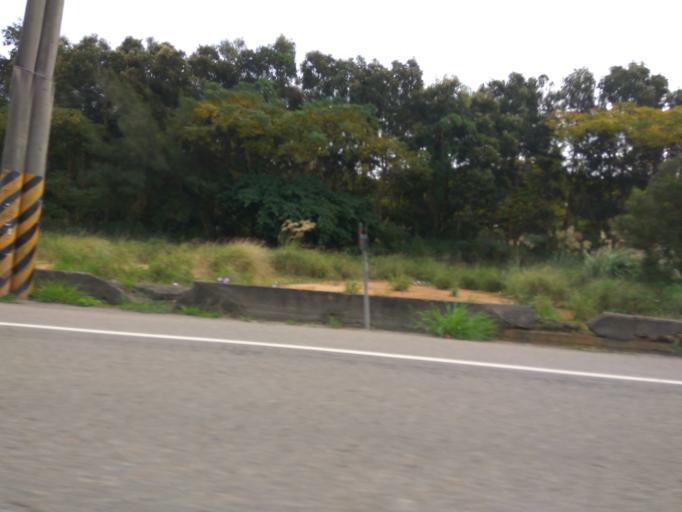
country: TW
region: Taiwan
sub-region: Hsinchu
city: Zhubei
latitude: 24.9560
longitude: 121.0123
